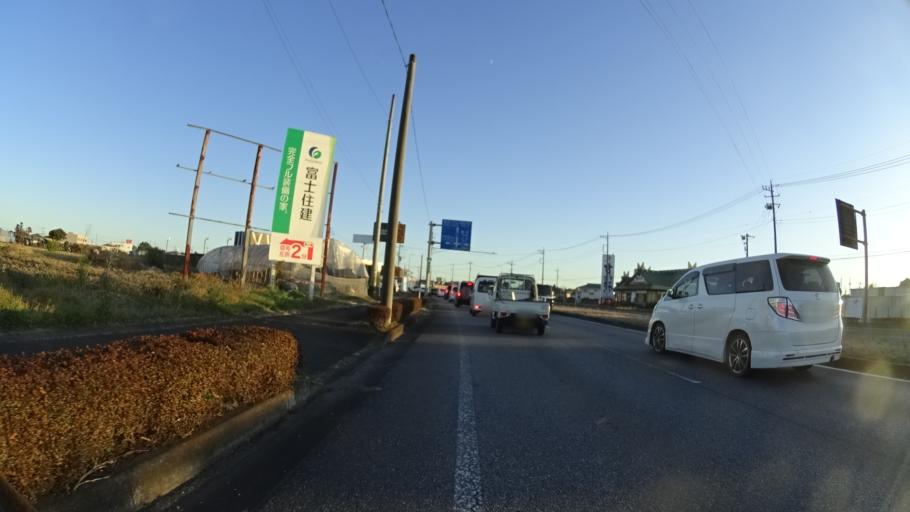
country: JP
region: Tochigi
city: Utsunomiya-shi
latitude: 36.5188
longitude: 139.8412
